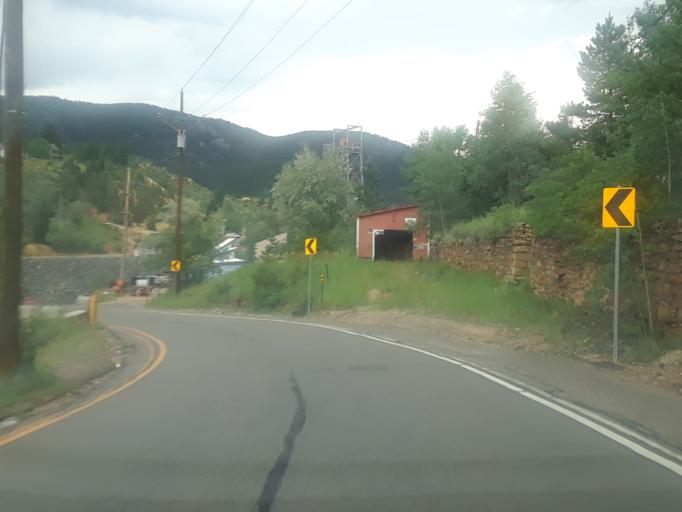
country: US
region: Colorado
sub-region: Gilpin County
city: Central City
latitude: 39.8002
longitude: -105.5049
